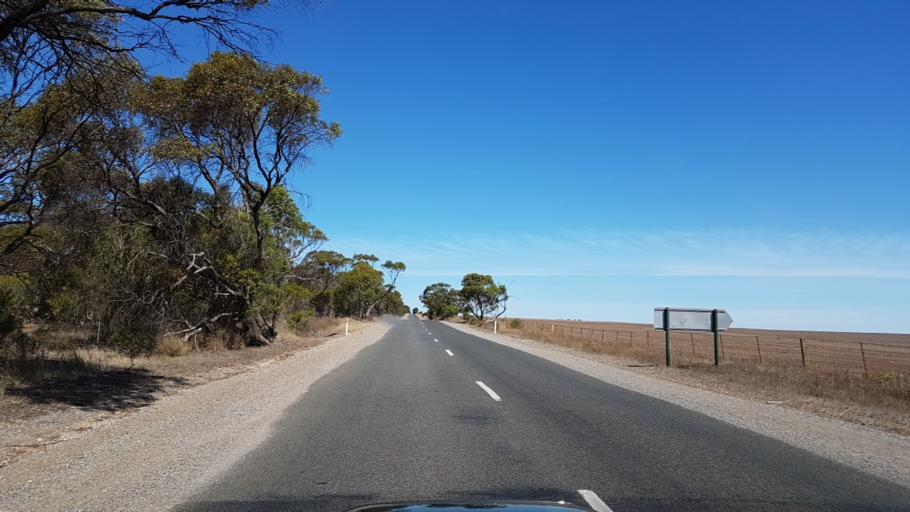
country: AU
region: South Australia
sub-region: Yorke Peninsula
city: Maitland
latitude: -34.3379
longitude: 137.6567
